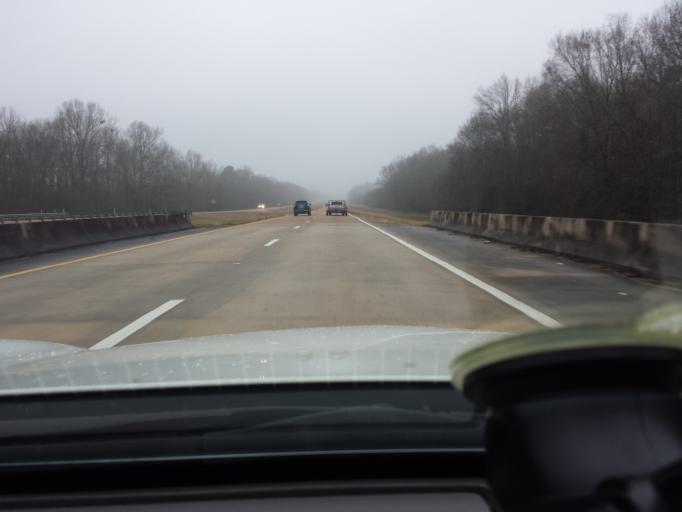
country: US
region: Mississippi
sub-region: Rankin County
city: Pelahatchie
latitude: 32.5324
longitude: -89.8274
